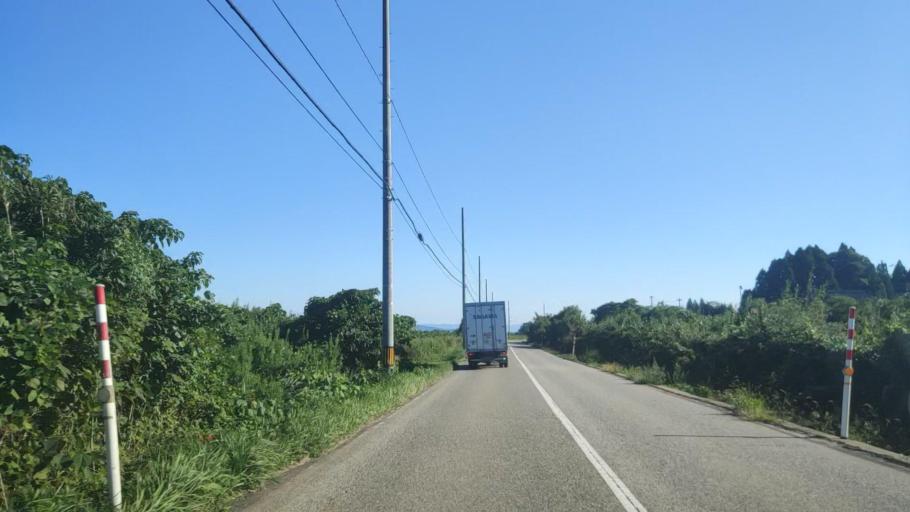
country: JP
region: Ishikawa
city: Nanao
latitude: 37.1967
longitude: 136.9103
